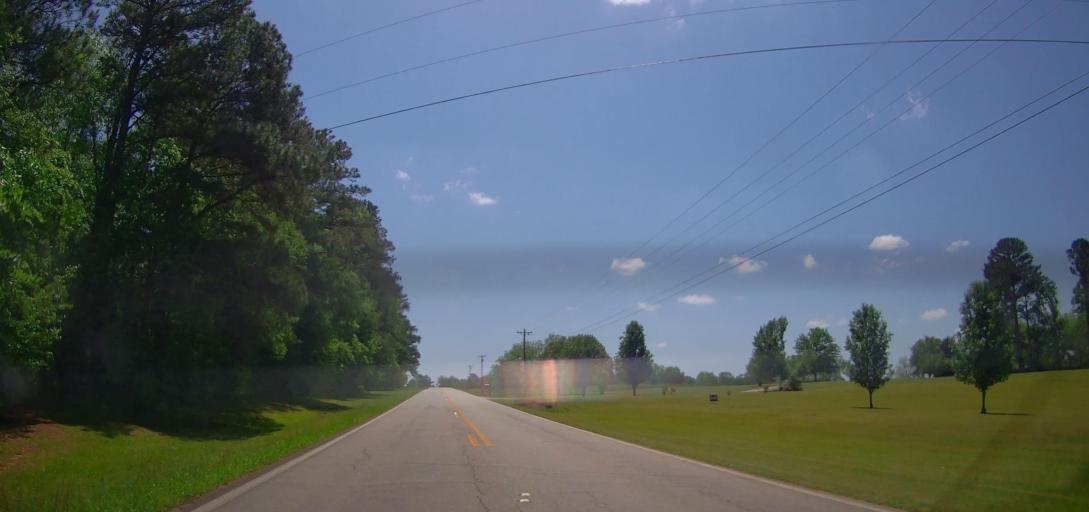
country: US
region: Georgia
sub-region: Jones County
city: Gray
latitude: 33.0446
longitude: -83.5923
